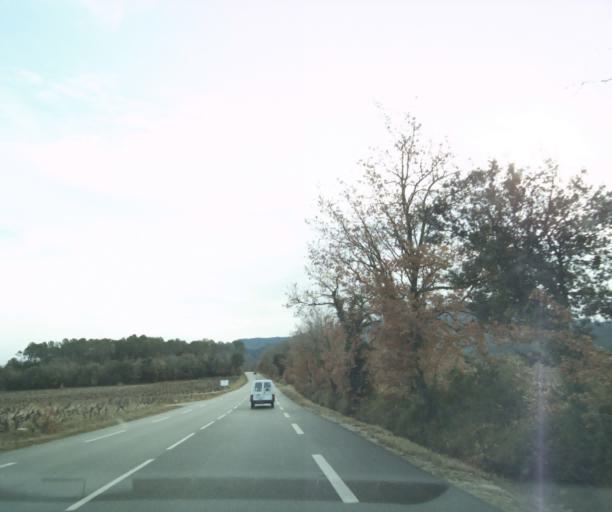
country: FR
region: Provence-Alpes-Cote d'Azur
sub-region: Departement du Var
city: Tourves
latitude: 43.3972
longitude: 5.9681
